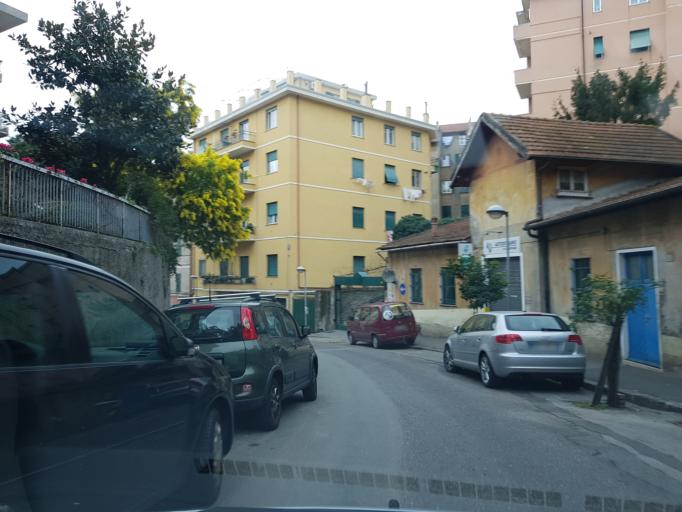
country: IT
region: Liguria
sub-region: Provincia di Genova
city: Mele
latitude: 44.4255
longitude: 8.8105
